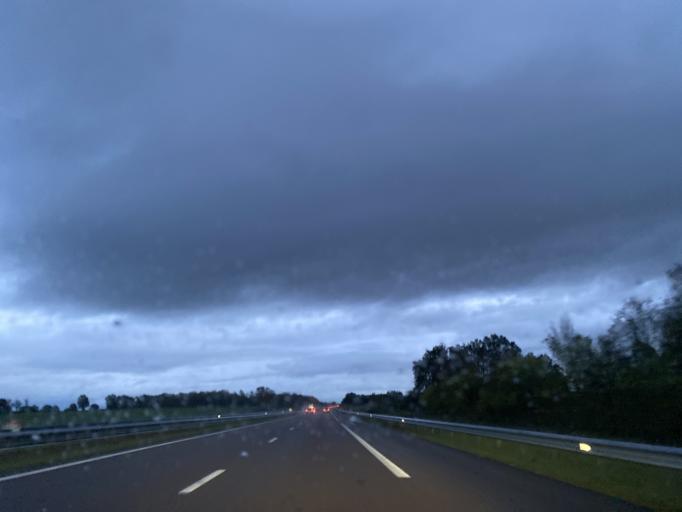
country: FR
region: Auvergne
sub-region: Departement de l'Allier
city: Estivareilles
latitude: 46.4733
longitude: 2.6745
